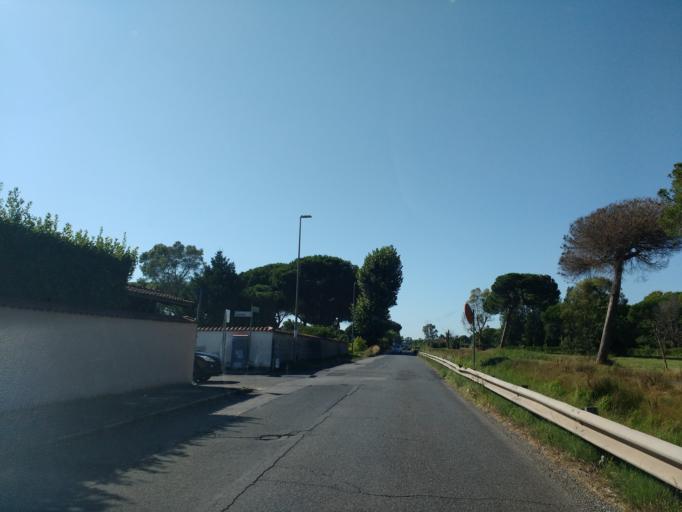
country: IT
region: Latium
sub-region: Citta metropolitana di Roma Capitale
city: Acilia-Castel Fusano-Ostia Antica
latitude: 41.7416
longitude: 12.3399
